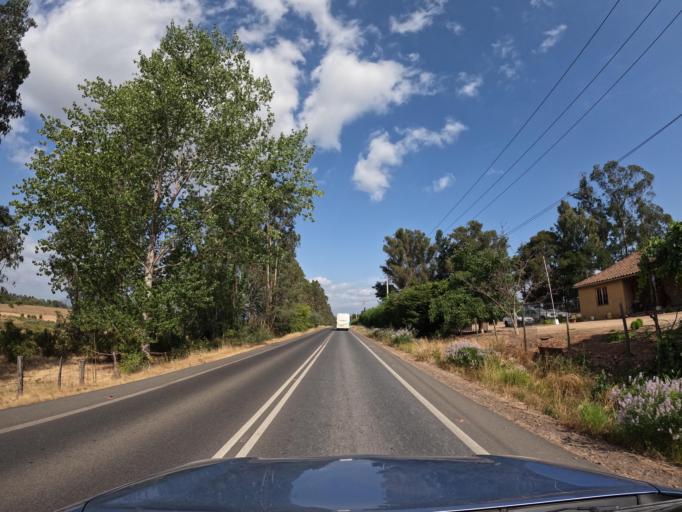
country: CL
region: Maule
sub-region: Provincia de Curico
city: Molina
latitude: -35.2717
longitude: -71.3069
